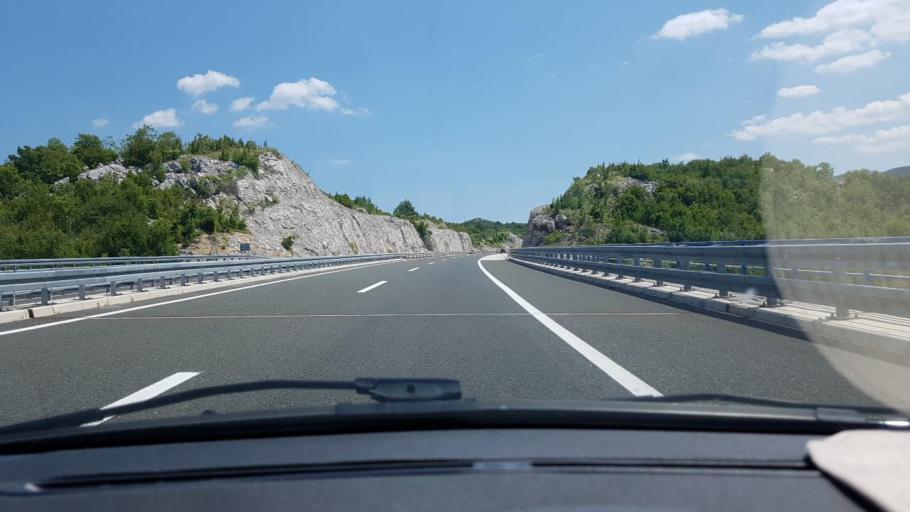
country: HR
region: Splitsko-Dalmatinska
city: Grubine
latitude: 43.3767
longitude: 17.0855
